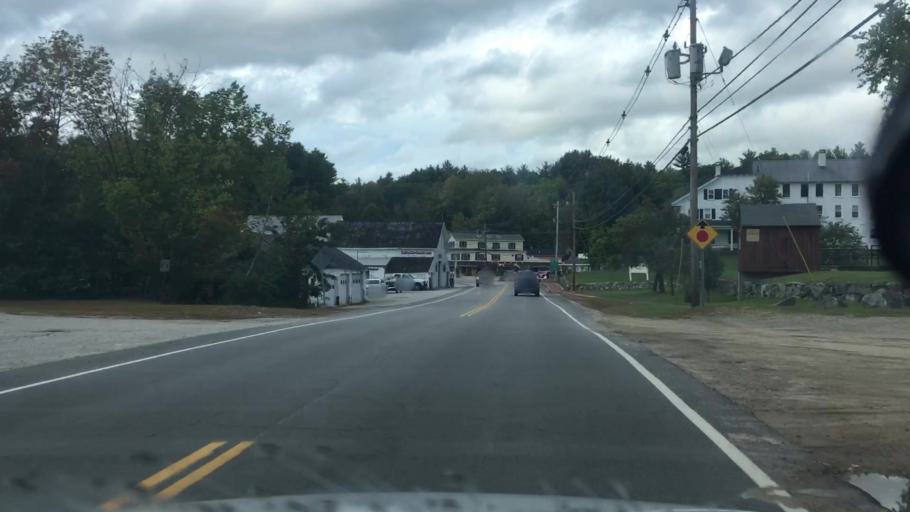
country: US
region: New Hampshire
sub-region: Carroll County
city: Sanbornville
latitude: 43.5523
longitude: -71.0258
